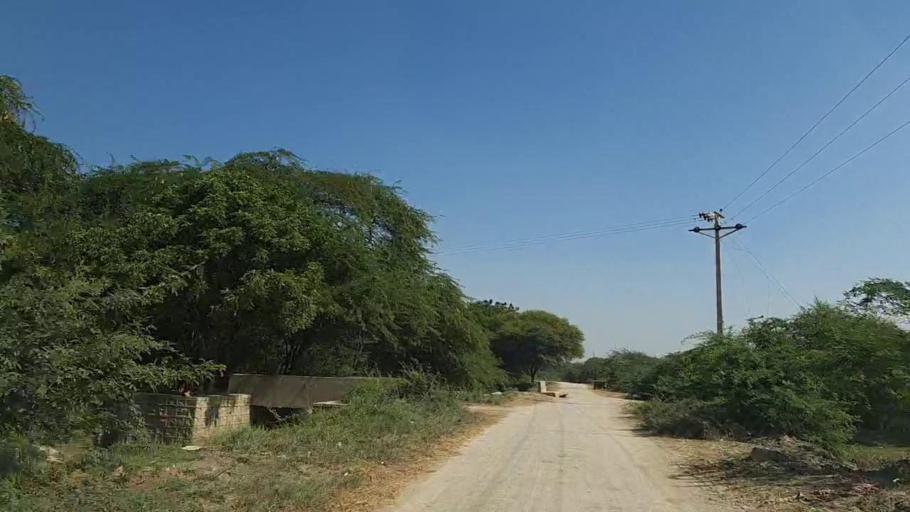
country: PK
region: Sindh
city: Daro Mehar
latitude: 24.7896
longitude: 68.1720
